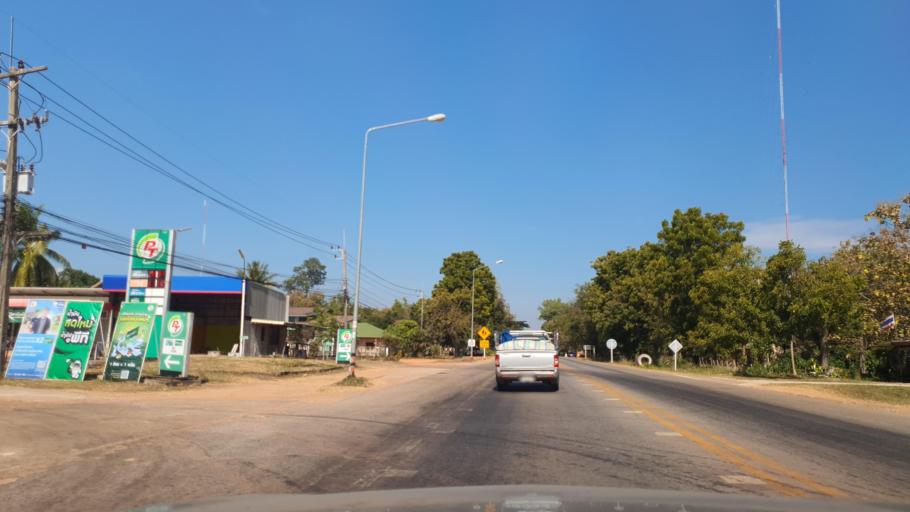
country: TH
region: Sakon Nakhon
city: Phu Phan
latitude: 17.0800
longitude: 103.9803
